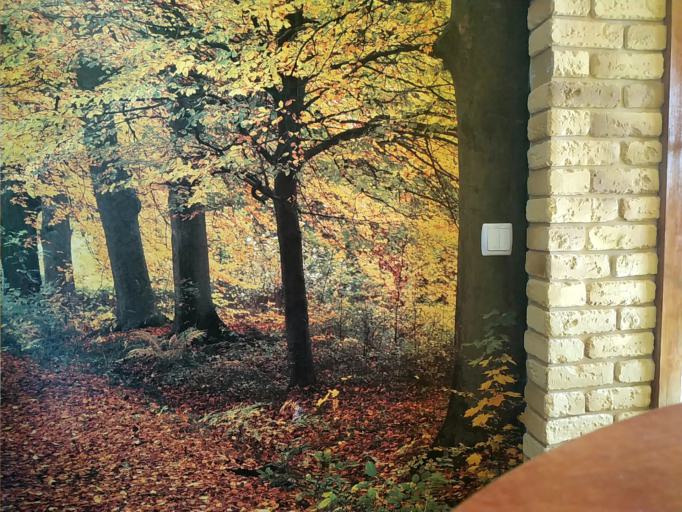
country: RU
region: Jaroslavl
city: Kukoboy
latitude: 58.8686
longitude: 39.7219
